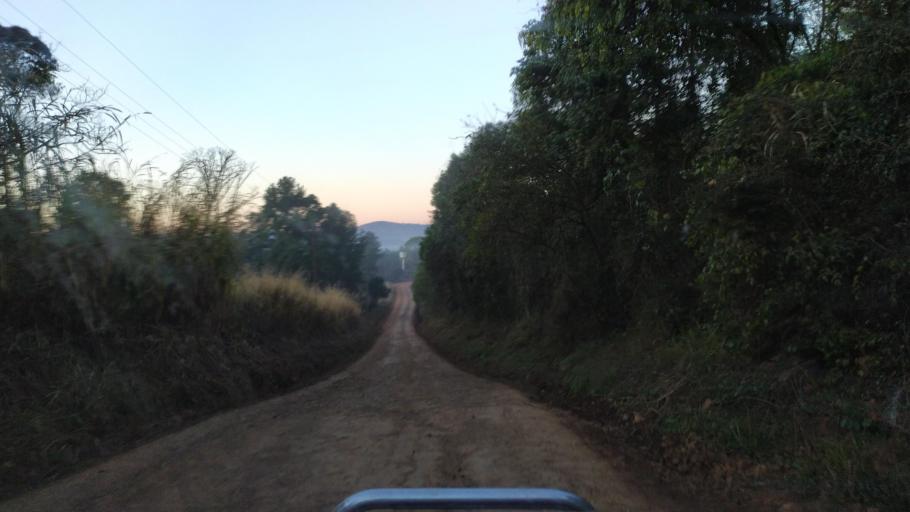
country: AR
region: Misiones
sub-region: Departamento de Montecarlo
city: Montecarlo
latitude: -26.6375
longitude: -54.6793
